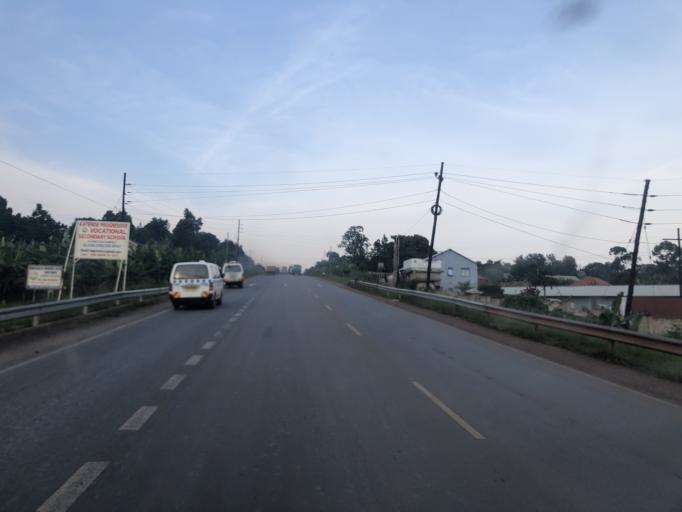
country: UG
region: Central Region
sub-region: Mpigi District
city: Mpigi
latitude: 0.2435
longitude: 32.3735
